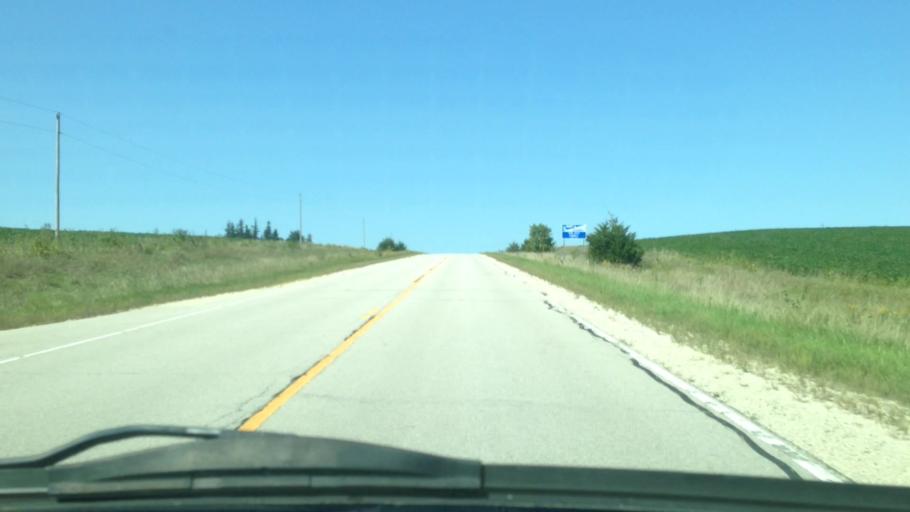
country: US
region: Minnesota
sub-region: Houston County
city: Spring Grove
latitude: 43.6343
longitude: -91.7903
